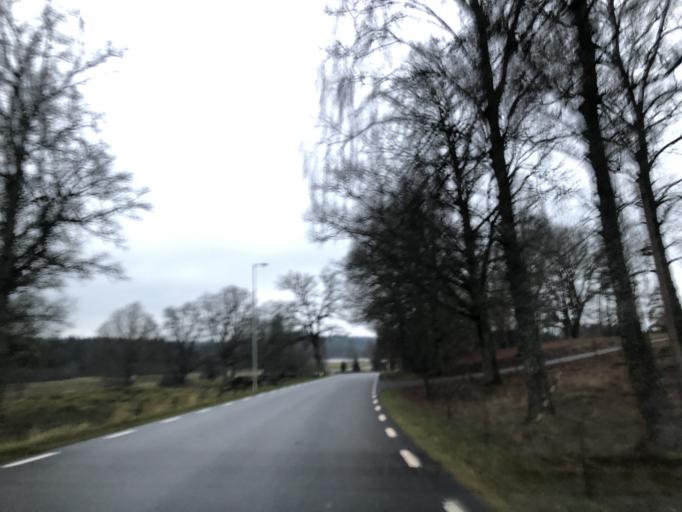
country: SE
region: Vaestra Goetaland
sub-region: Boras Kommun
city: Dalsjofors
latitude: 57.8345
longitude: 13.2173
